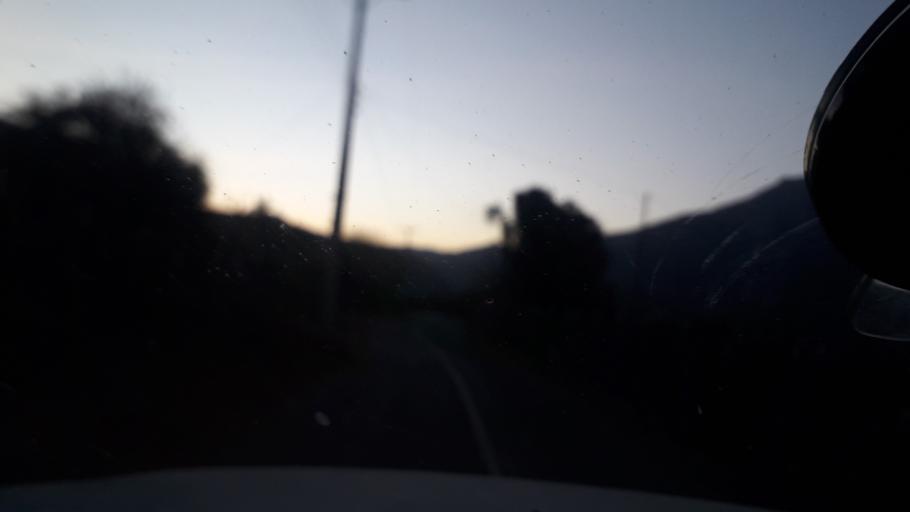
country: CL
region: Valparaiso
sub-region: Provincia de Marga Marga
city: Limache
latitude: -33.1777
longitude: -71.1186
